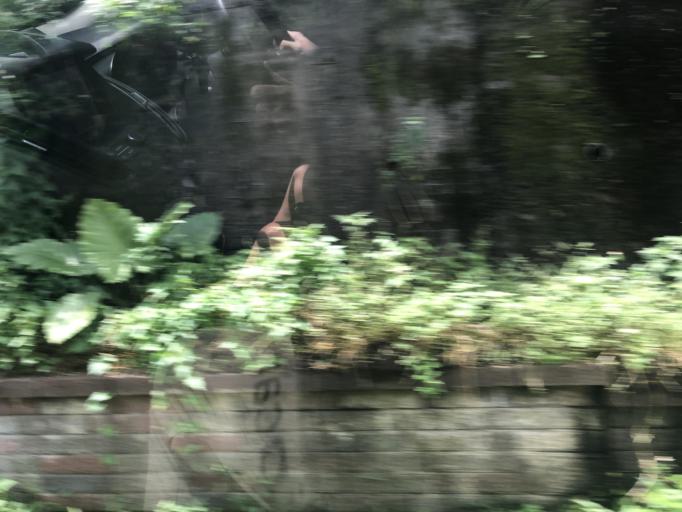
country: TW
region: Taipei
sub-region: Taipei
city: Banqiao
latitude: 24.9204
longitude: 121.4237
